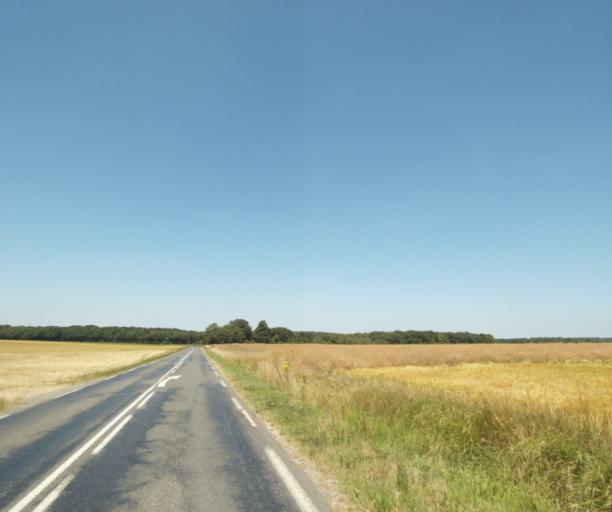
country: FR
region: Ile-de-France
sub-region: Departement de l'Essonne
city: Milly-la-Foret
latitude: 48.3518
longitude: 2.4552
